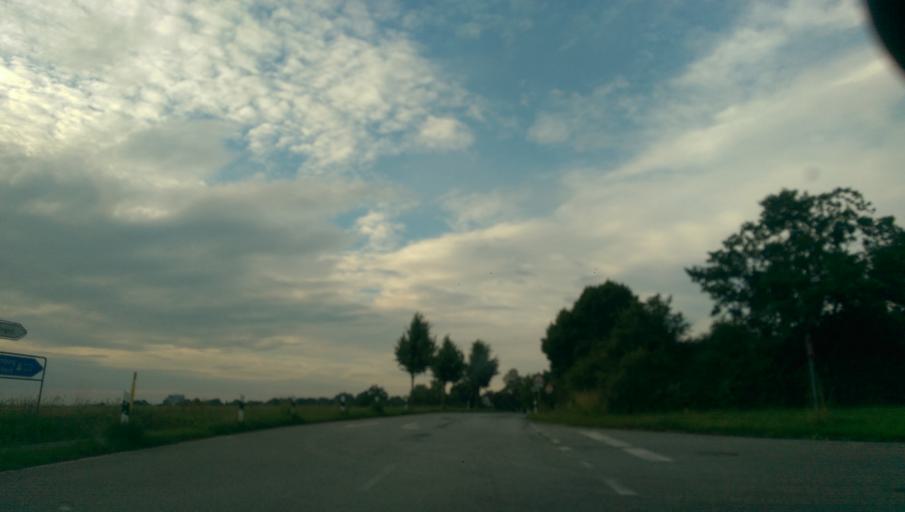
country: DE
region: Schleswig-Holstein
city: Reinfeld
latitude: 53.8214
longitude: 10.4934
